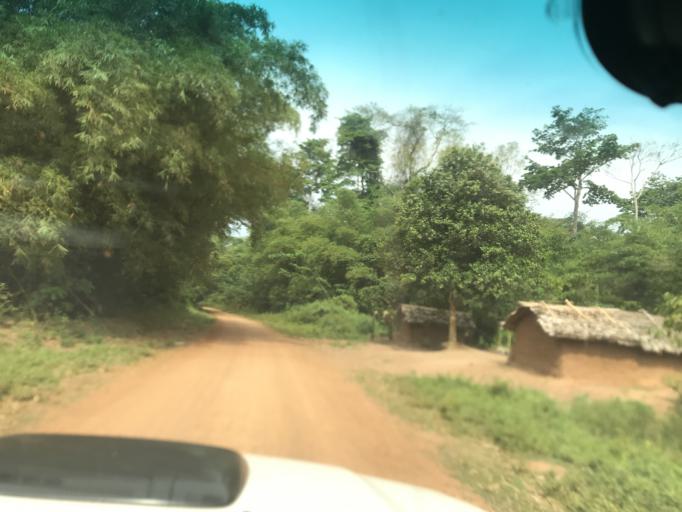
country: CD
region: Eastern Province
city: Buta
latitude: 2.8788
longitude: 24.4697
